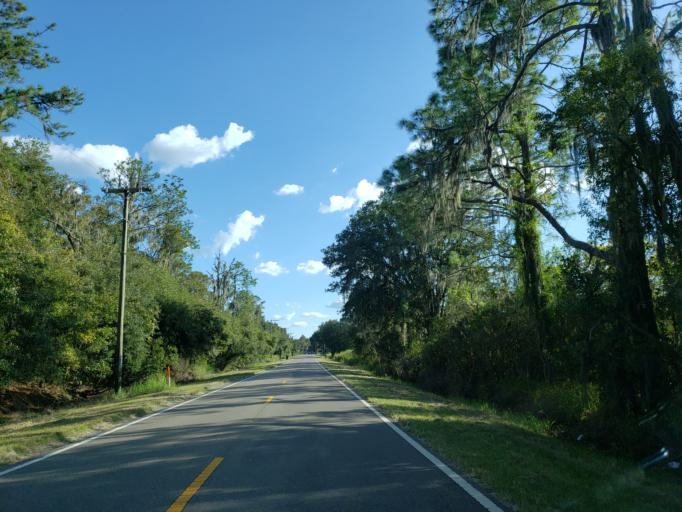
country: US
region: Florida
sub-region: Hillsborough County
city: Valrico
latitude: 27.9509
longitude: -82.2196
